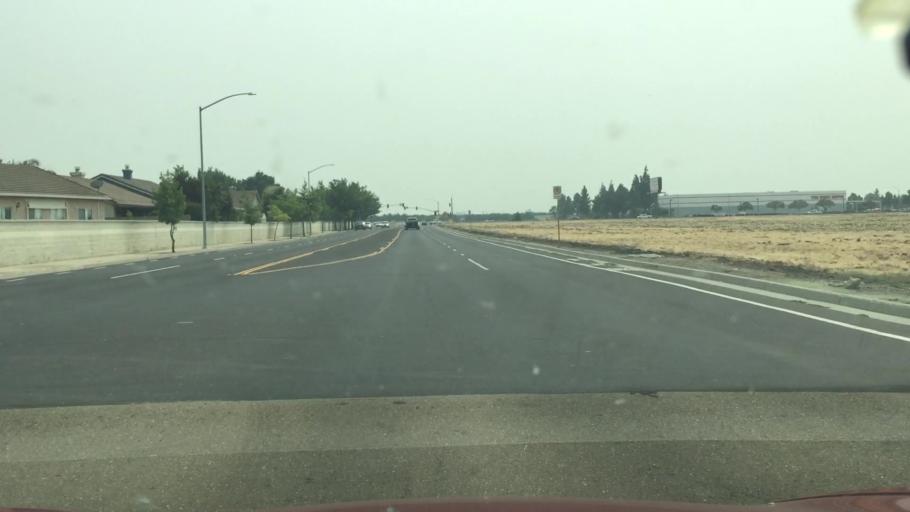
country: US
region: California
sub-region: San Joaquin County
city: Morada
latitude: 38.0243
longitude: -121.2642
